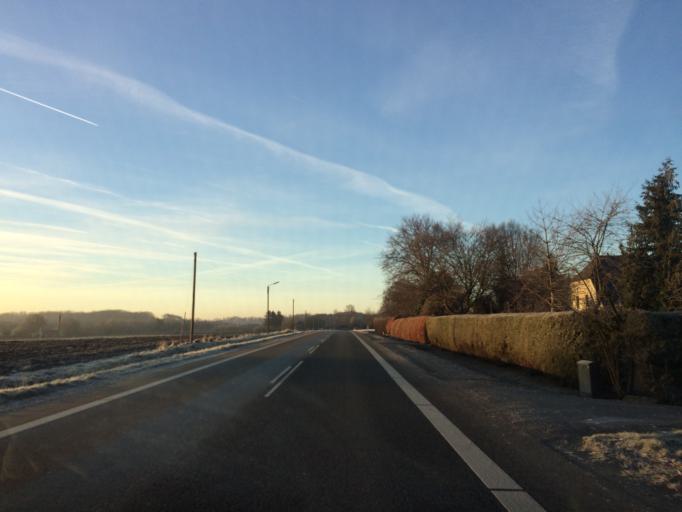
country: DK
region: South Denmark
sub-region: Odense Kommune
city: Bellinge
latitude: 55.3100
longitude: 10.3094
